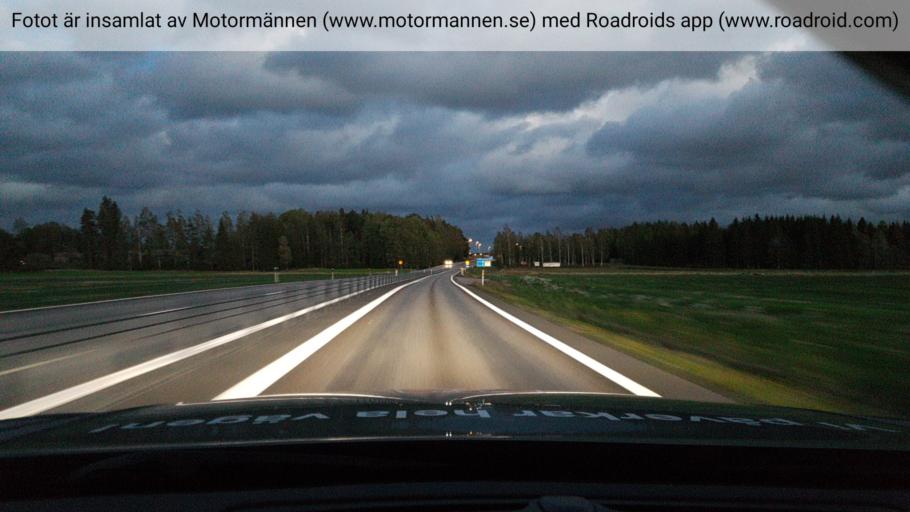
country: SE
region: Vaermland
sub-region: Kristinehamns Kommun
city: Kristinehamn
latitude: 59.3725
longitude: 14.0033
